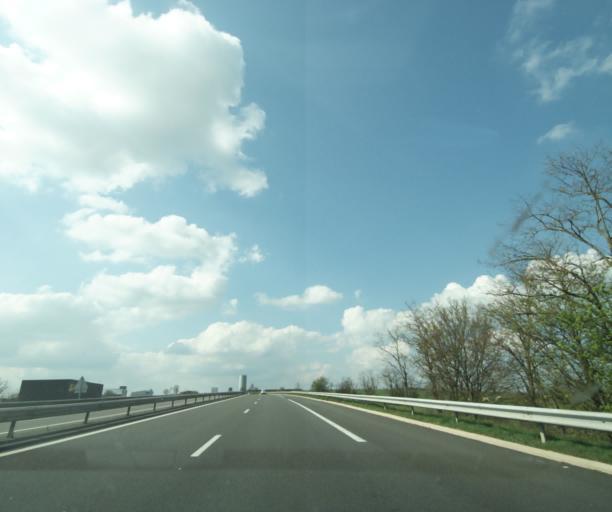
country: FR
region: Auvergne
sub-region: Departement de l'Allier
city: Montmarault
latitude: 46.3240
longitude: 2.9815
